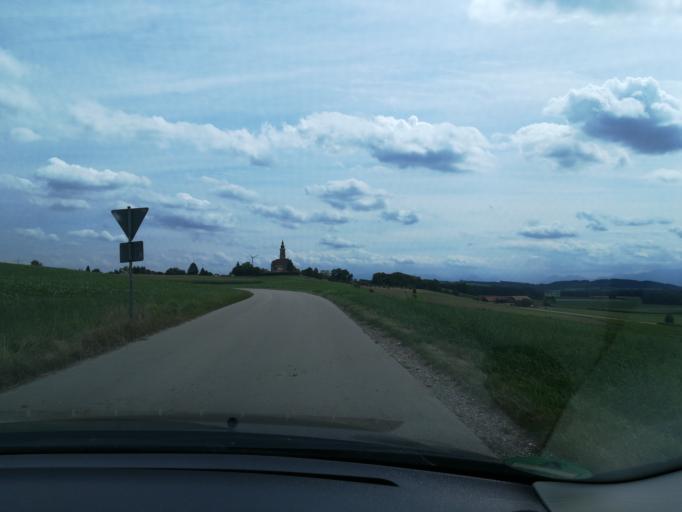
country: DE
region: Bavaria
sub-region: Upper Bavaria
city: Bruck
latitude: 48.0266
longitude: 11.9208
